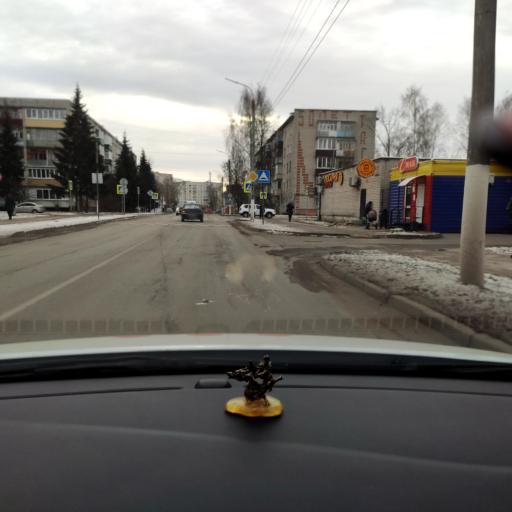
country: RU
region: Tatarstan
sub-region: Zelenodol'skiy Rayon
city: Zelenodolsk
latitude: 55.8498
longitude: 48.5250
